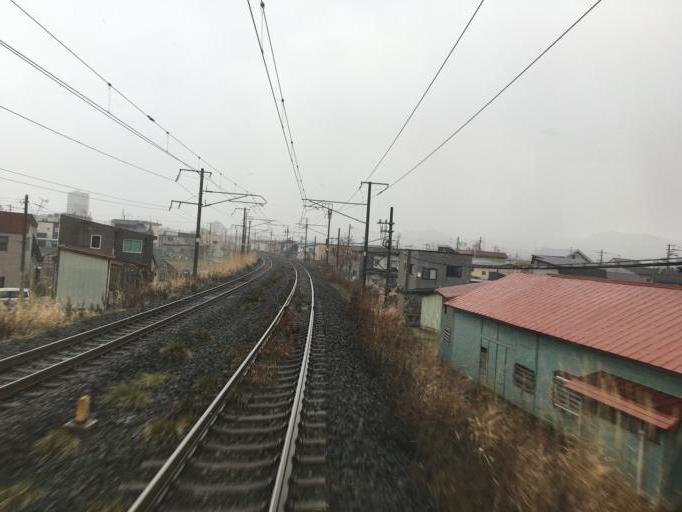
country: JP
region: Aomori
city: Aomori Shi
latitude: 40.8060
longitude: 140.7739
